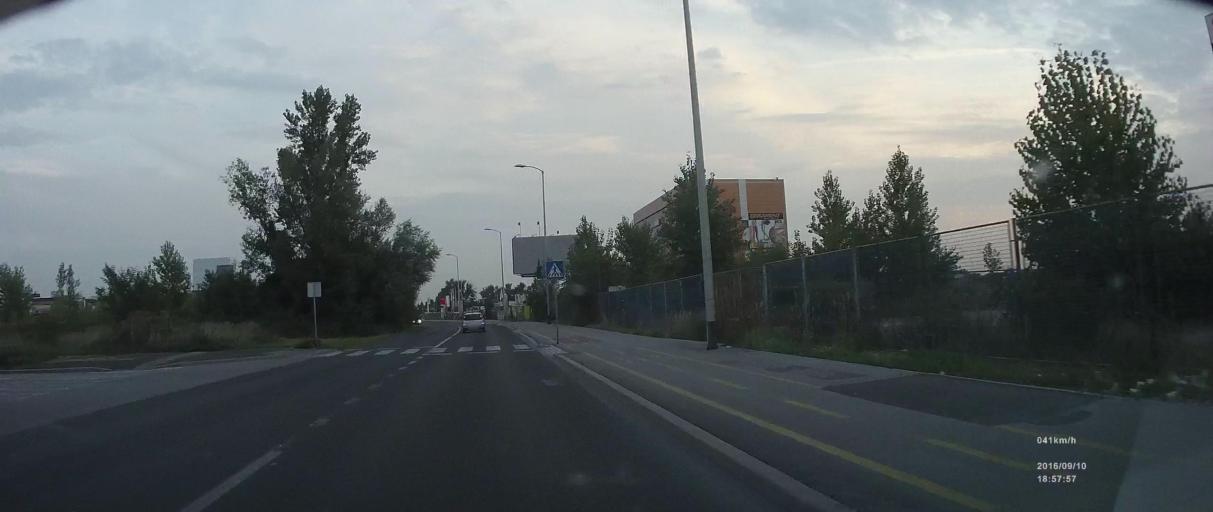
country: HR
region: Grad Zagreb
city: Novi Zagreb
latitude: 45.7634
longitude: 15.9810
